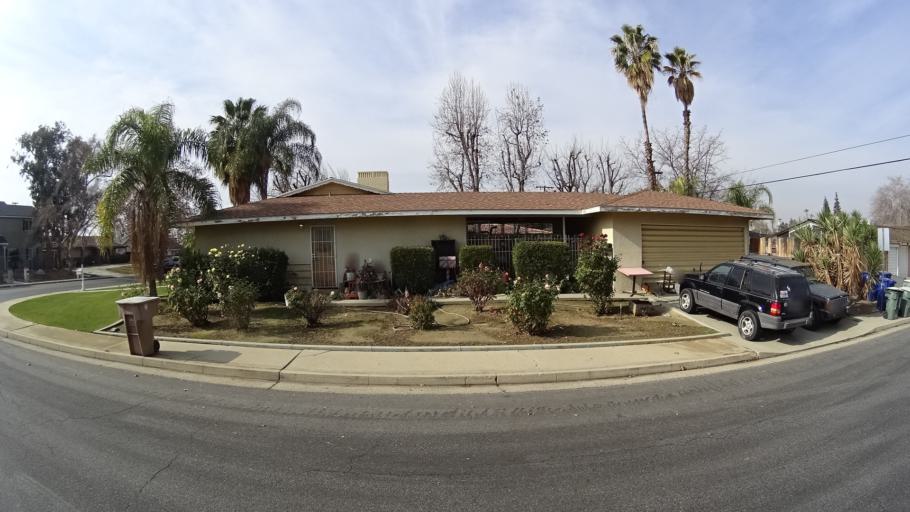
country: US
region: California
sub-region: Kern County
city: Oildale
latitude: 35.4090
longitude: -118.9587
